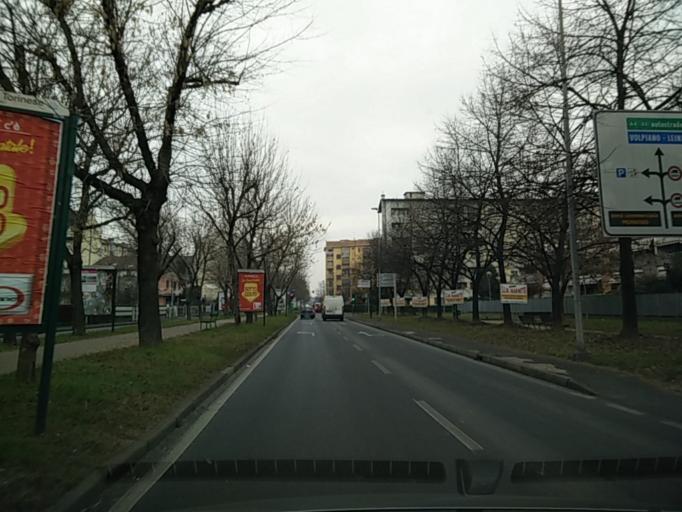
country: IT
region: Piedmont
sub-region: Provincia di Torino
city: Settimo Torinese
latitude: 45.1393
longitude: 7.7570
